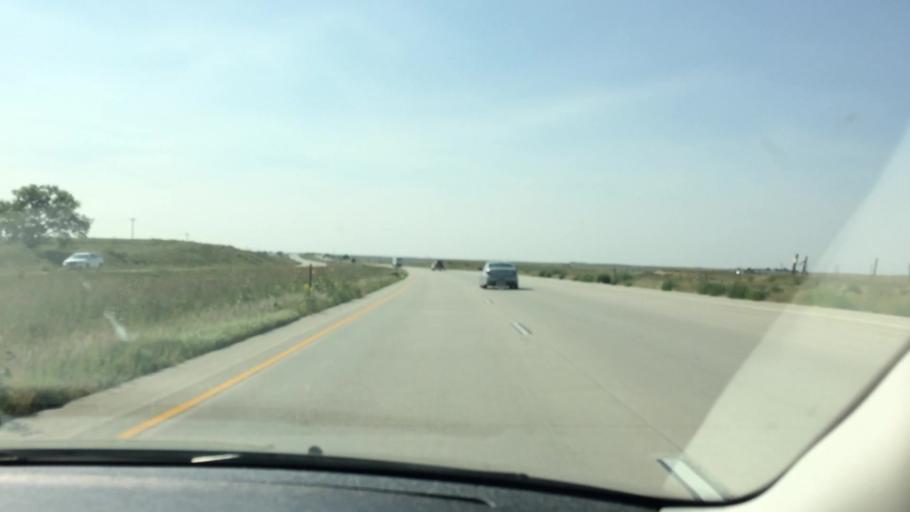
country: US
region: Colorado
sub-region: Arapahoe County
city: Byers
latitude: 39.6855
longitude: -104.1213
